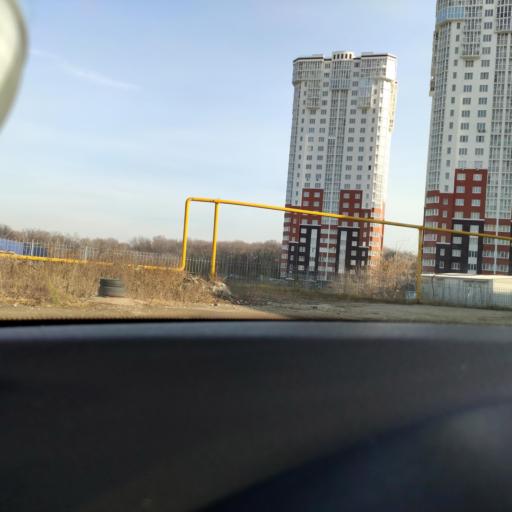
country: RU
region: Samara
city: Petra-Dubrava
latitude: 53.2768
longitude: 50.2761
